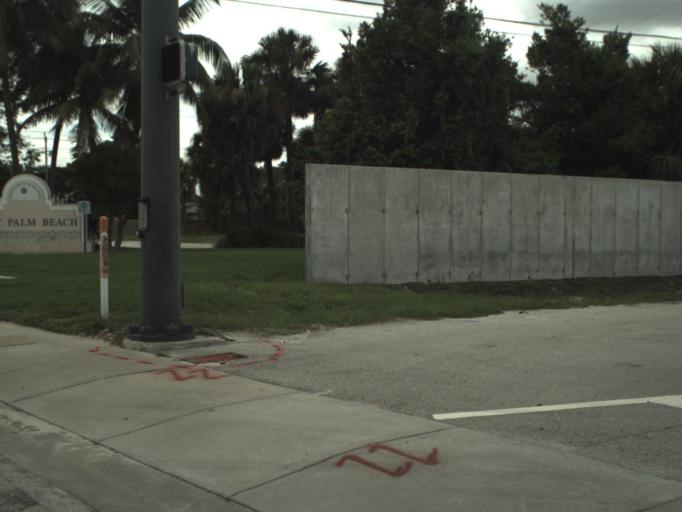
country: US
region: Florida
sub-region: Palm Beach County
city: Riviera Beach
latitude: 26.7636
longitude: -80.0553
